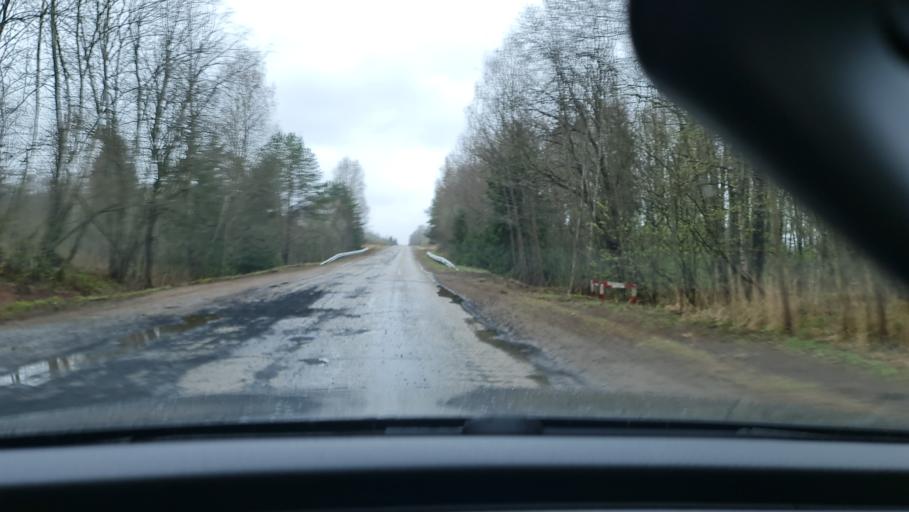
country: RU
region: Novgorod
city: Valday
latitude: 58.0359
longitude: 32.8852
